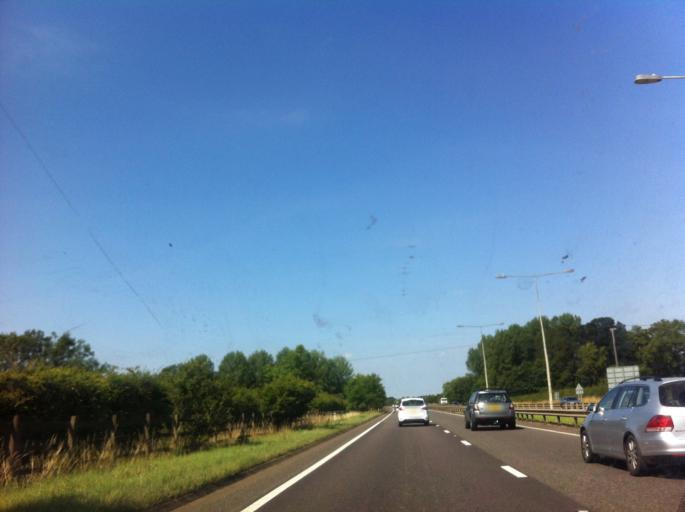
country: GB
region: England
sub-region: Northamptonshire
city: Earls Barton
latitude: 52.2547
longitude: -0.7625
